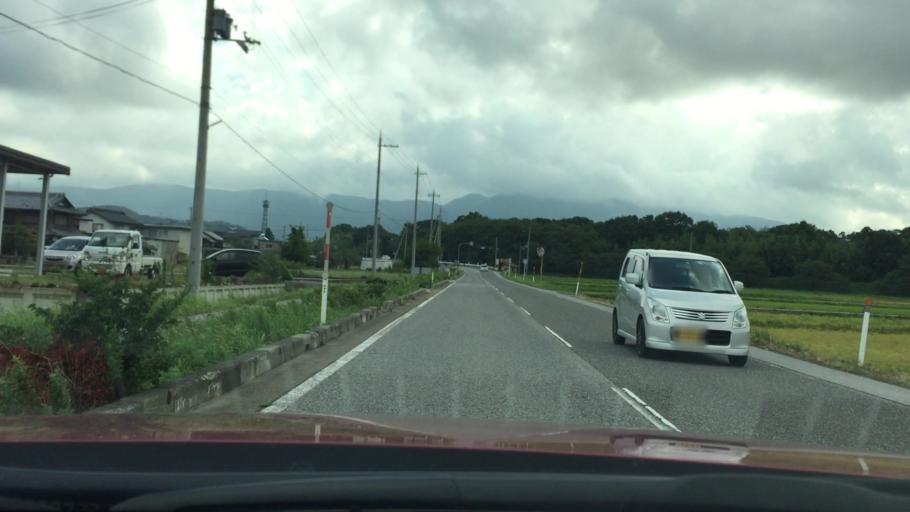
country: JP
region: Shiga Prefecture
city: Nagahama
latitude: 35.4249
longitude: 136.2916
